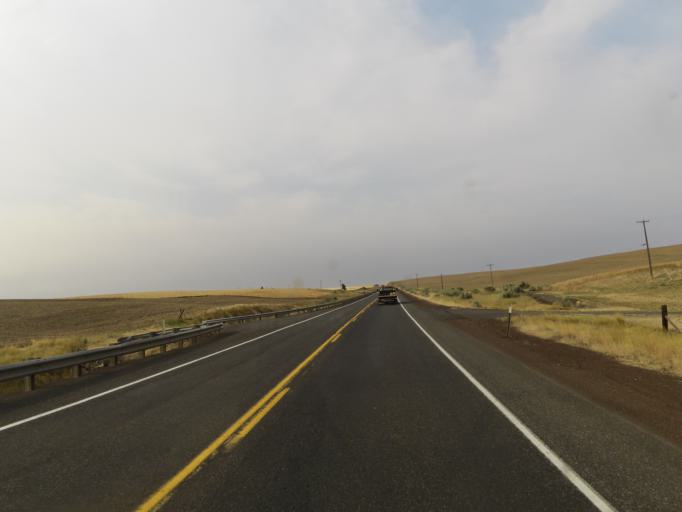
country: US
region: Oregon
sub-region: Sherman County
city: Moro
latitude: 45.4451
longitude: -120.7544
